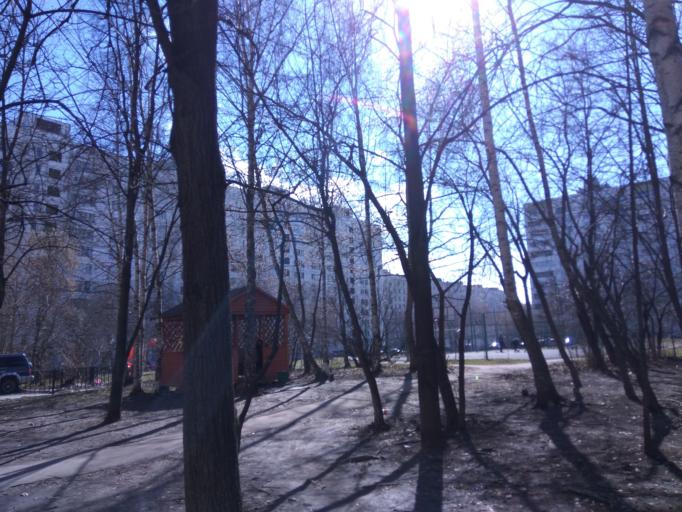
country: RU
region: Moscow
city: Ivanovskoye
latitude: 55.7804
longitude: 37.8345
